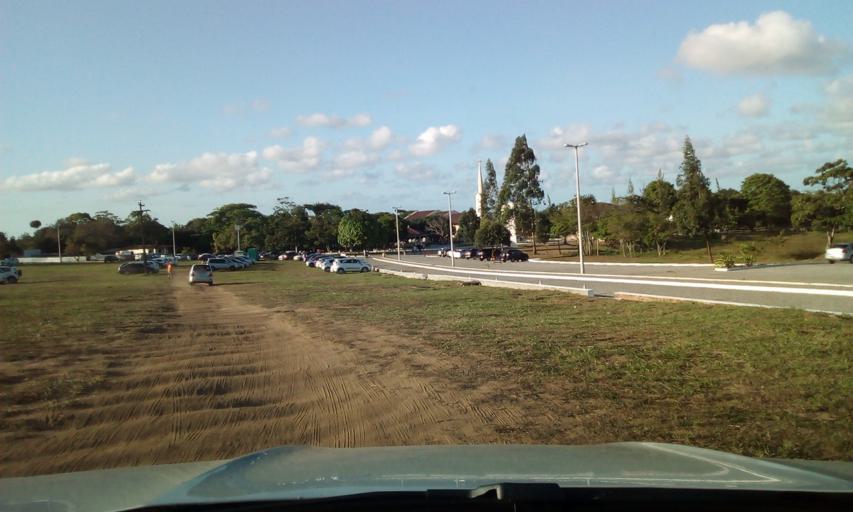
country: BR
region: Paraiba
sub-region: Conde
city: Conde
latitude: -7.2255
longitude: -34.9174
